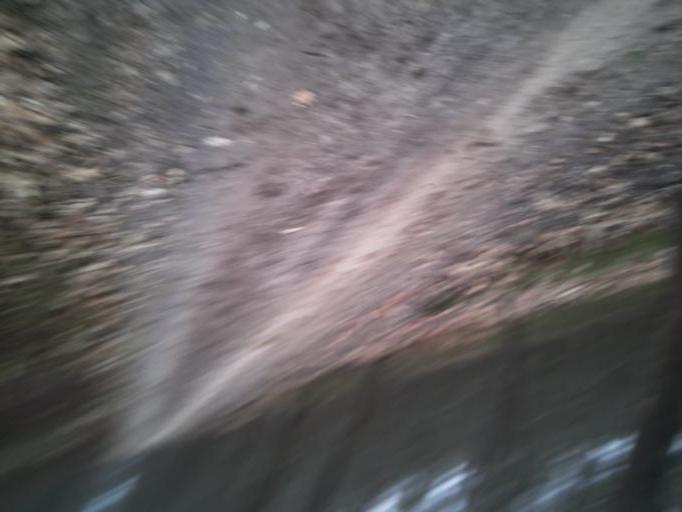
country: NL
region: Gelderland
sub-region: Gemeente Apeldoorn
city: Beekbergen
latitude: 52.1587
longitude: 5.9347
